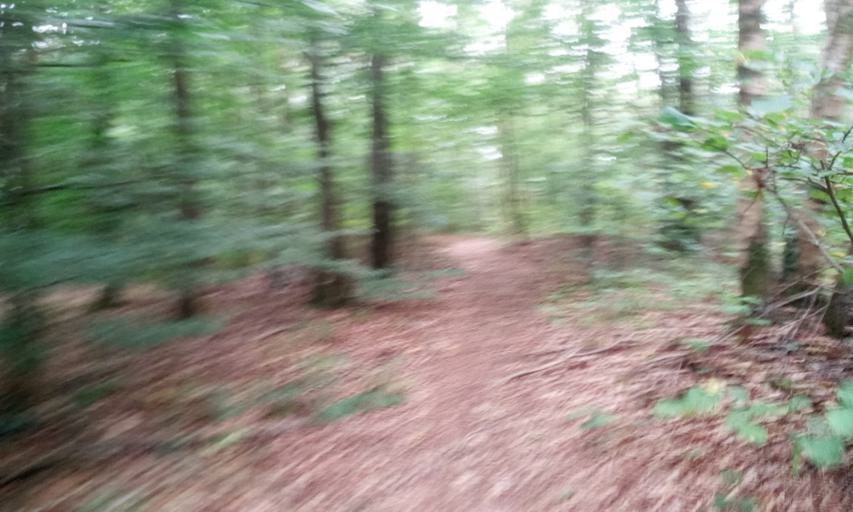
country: FR
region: Lower Normandy
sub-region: Departement du Calvados
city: Mouen
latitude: 49.1415
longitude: -0.4802
